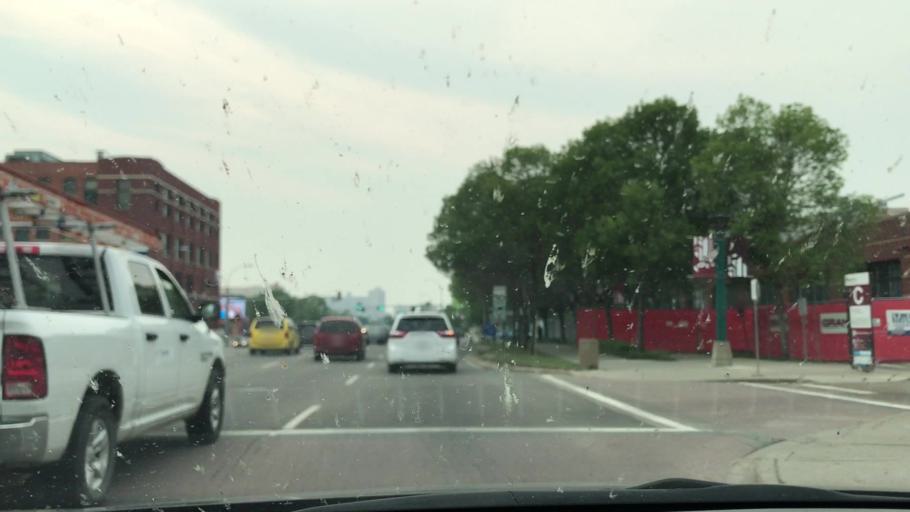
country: CA
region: Alberta
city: Edmonton
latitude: 53.5463
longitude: -113.5064
